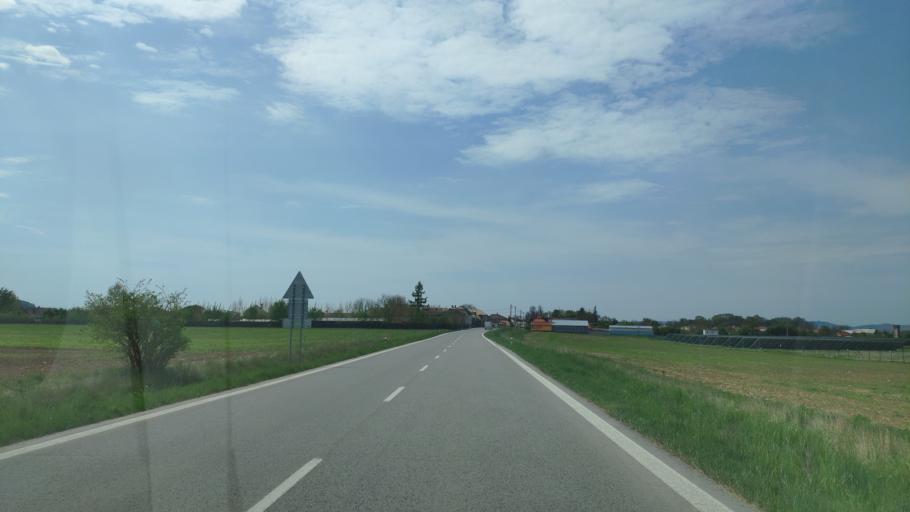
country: HU
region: Borsod-Abauj-Zemplen
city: Putnok
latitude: 48.4449
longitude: 20.3367
